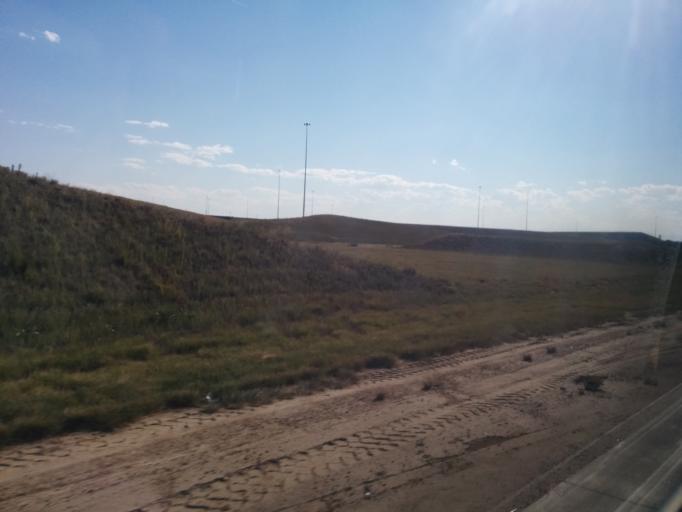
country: US
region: Colorado
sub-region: Adams County
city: Aurora
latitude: 39.8346
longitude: -104.7412
